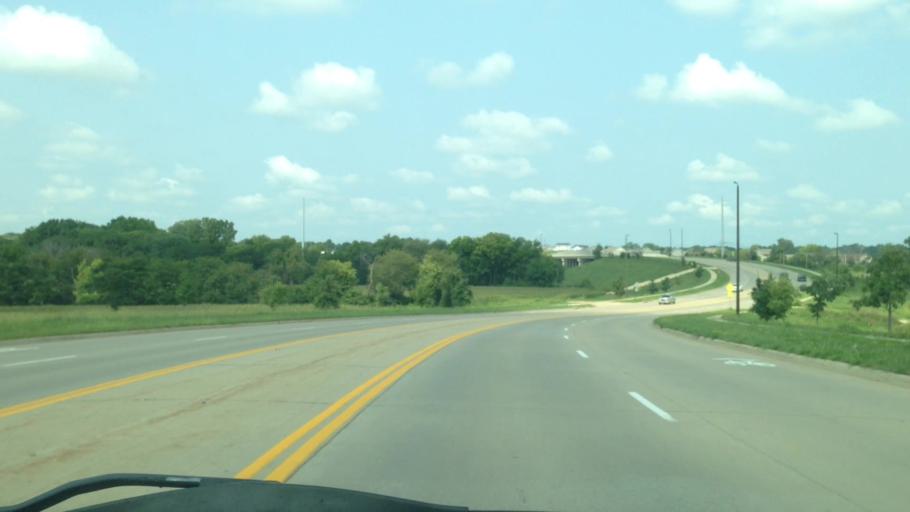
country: US
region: Iowa
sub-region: Linn County
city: Cedar Rapids
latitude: 41.9436
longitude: -91.6892
